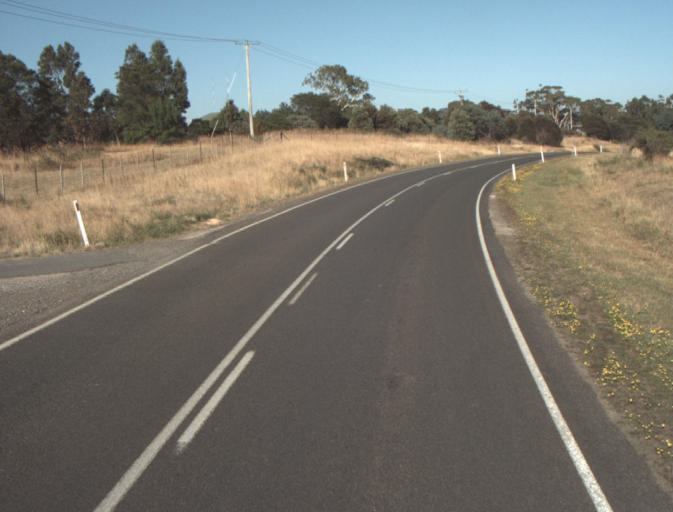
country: AU
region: Tasmania
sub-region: Launceston
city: Newstead
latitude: -41.4465
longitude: 147.2276
